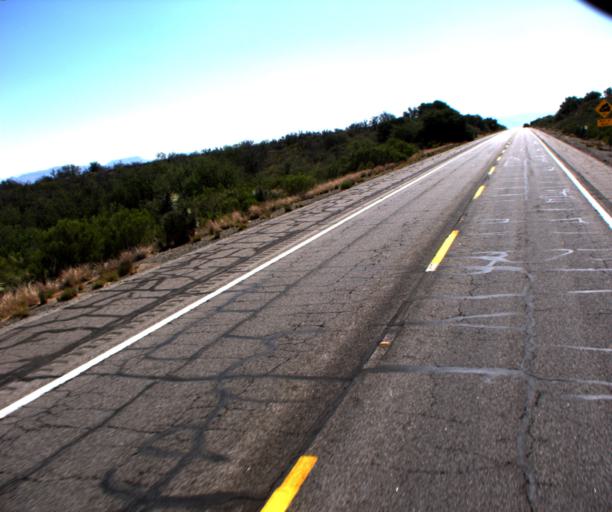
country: US
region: Arizona
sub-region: Pinal County
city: Oracle
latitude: 32.6235
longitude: -110.7647
